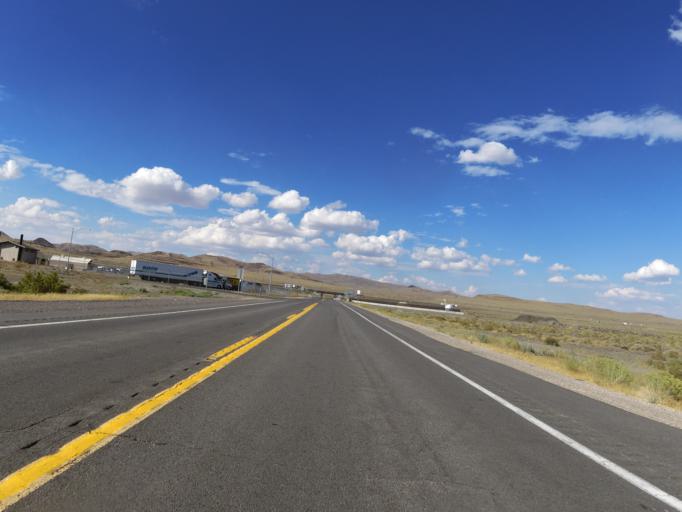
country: US
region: Nevada
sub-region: Pershing County
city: Lovelock
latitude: 39.9383
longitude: -118.7491
